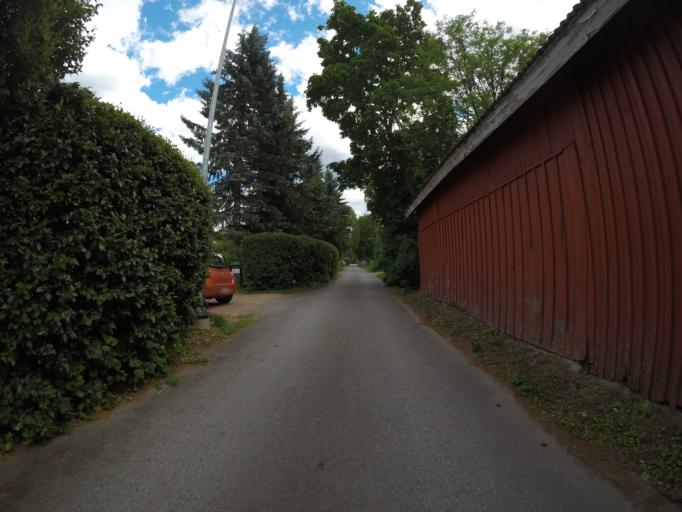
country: FI
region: Haeme
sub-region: Haemeenlinna
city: Haemeenlinna
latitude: 60.9971
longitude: 24.4317
